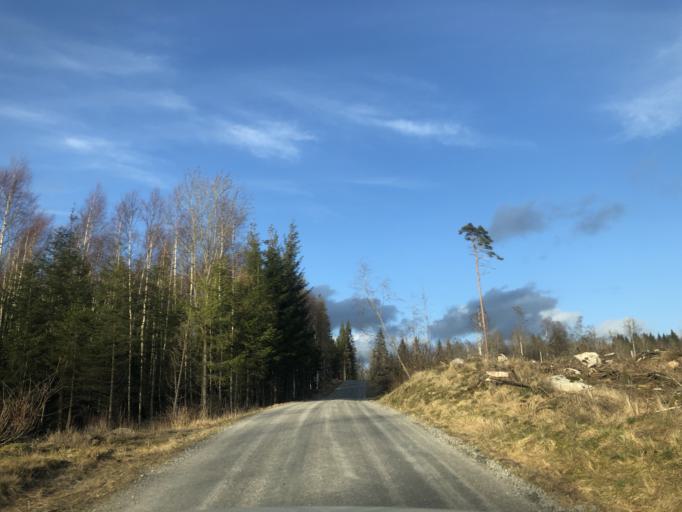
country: SE
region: Vaestra Goetaland
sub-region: Ulricehamns Kommun
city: Ulricehamn
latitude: 57.7638
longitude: 13.4644
